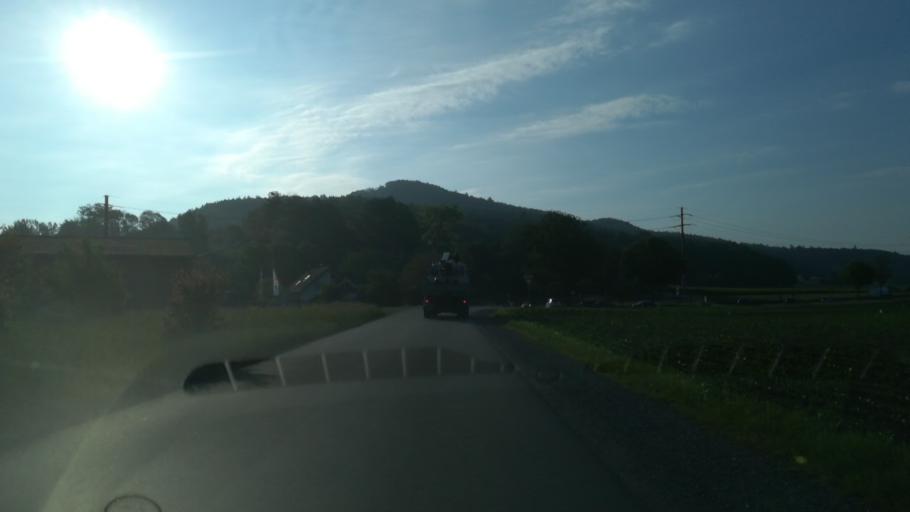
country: CH
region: Schaffhausen
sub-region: Bezirk Stein
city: Ramsen
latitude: 47.7045
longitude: 8.8189
